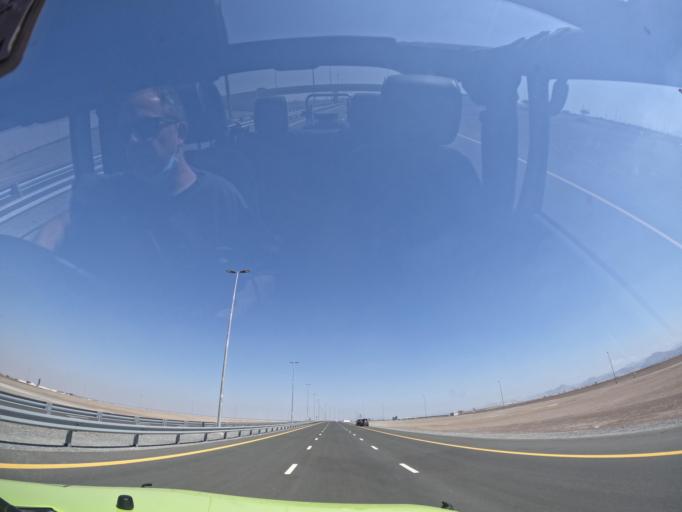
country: AE
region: Ash Shariqah
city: Adh Dhayd
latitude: 25.1099
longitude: 55.9334
